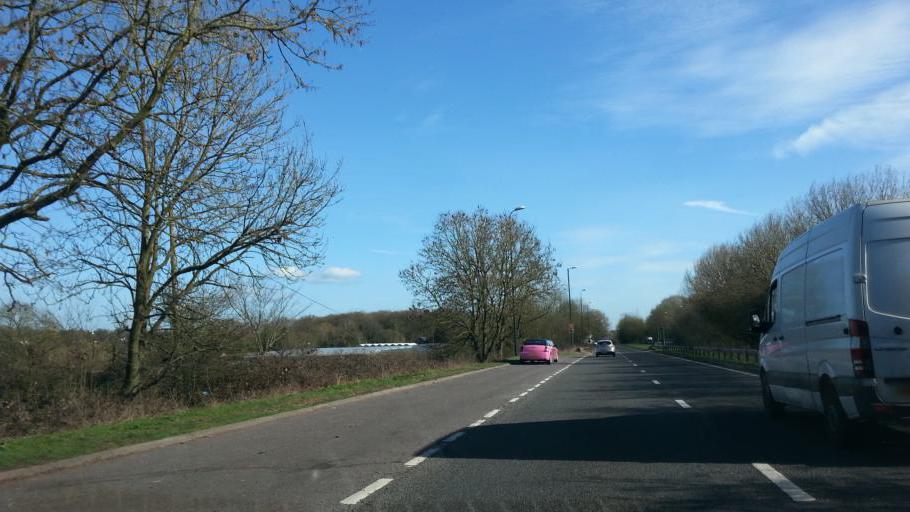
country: GB
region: England
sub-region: Solihull
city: Meriden
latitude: 52.4353
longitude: -1.6043
